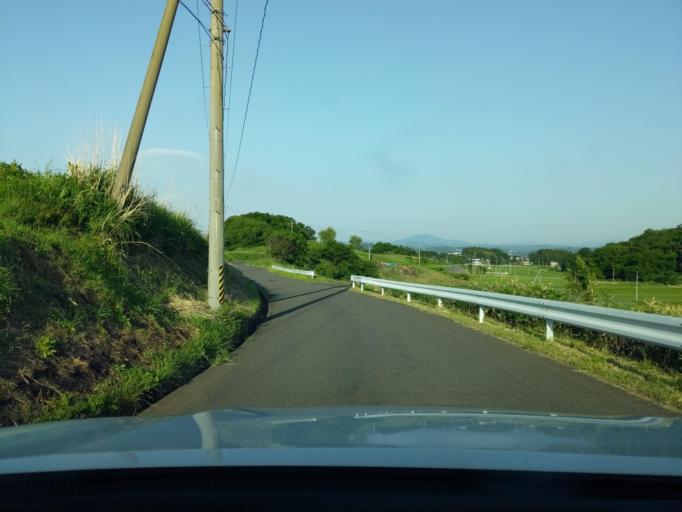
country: JP
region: Fukushima
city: Motomiya
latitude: 37.5369
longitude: 140.3530
